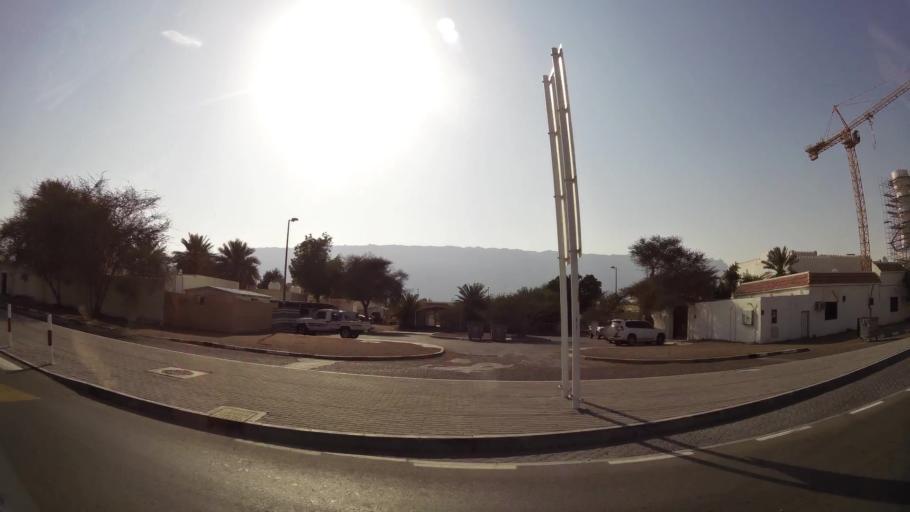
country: AE
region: Abu Dhabi
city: Al Ain
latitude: 24.0355
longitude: 55.8444
